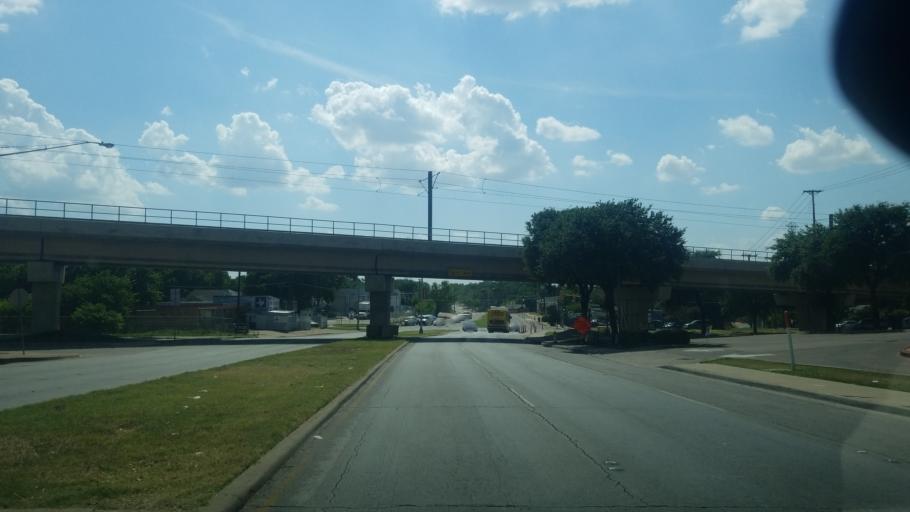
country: US
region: Texas
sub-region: Dallas County
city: Dallas
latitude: 32.7201
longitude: -96.8043
